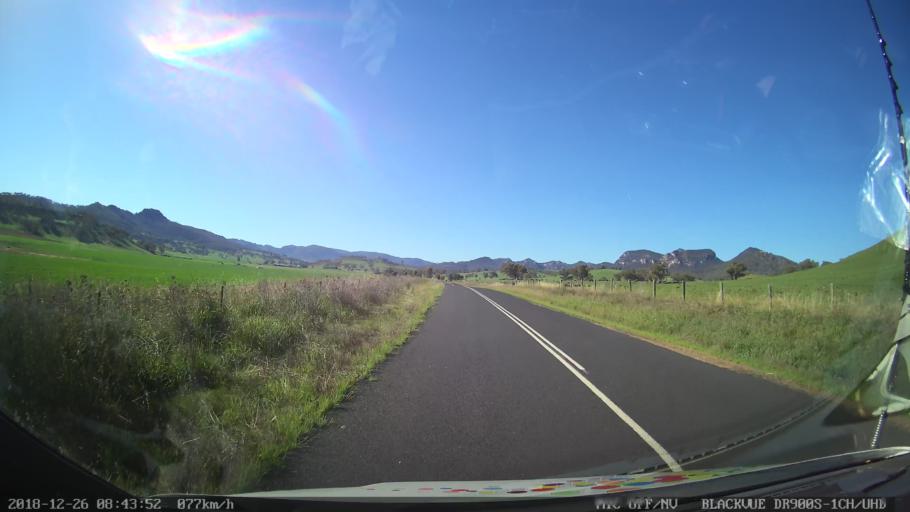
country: AU
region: New South Wales
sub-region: Mid-Western Regional
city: Kandos
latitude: -32.5077
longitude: 150.0805
